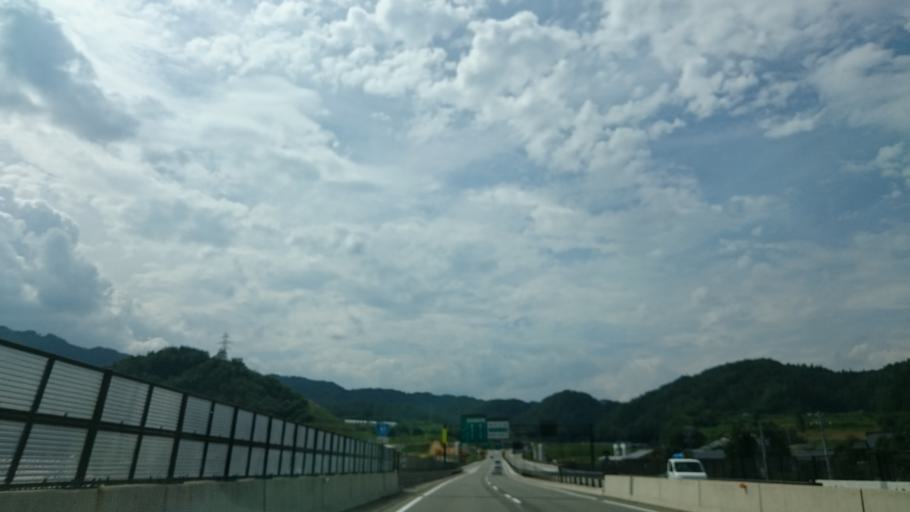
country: JP
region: Gifu
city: Takayama
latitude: 36.1646
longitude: 137.2335
